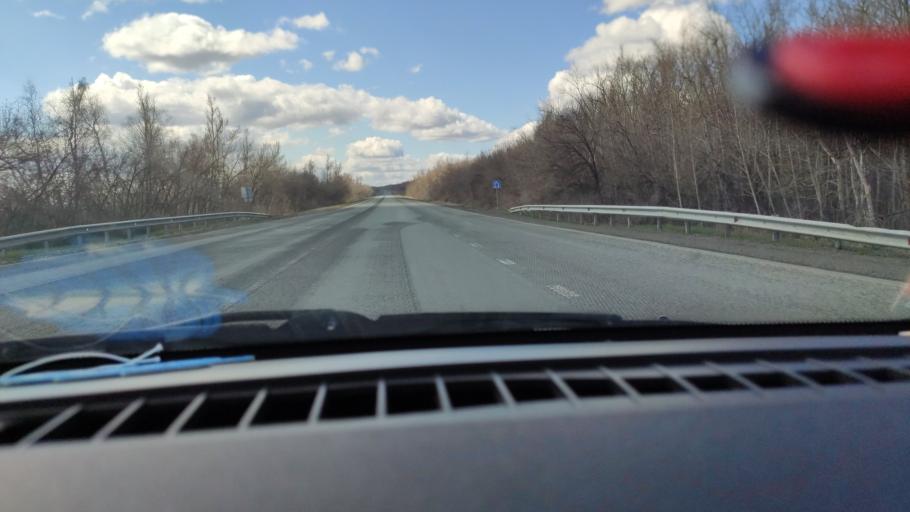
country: RU
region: Saratov
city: Dukhovnitskoye
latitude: 52.6554
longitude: 48.2048
